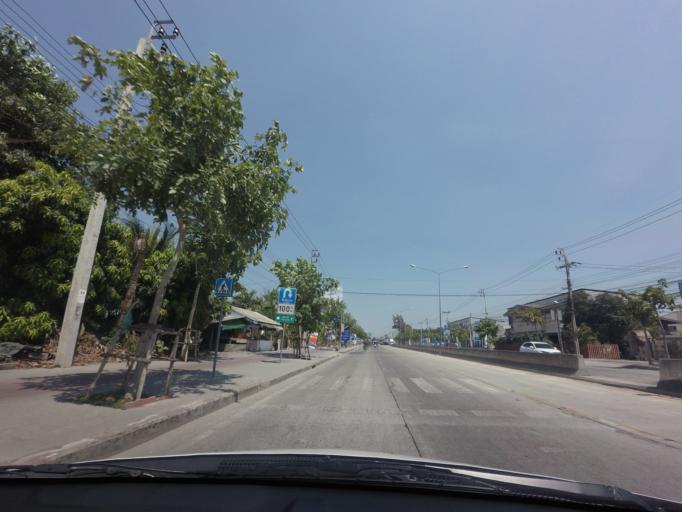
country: TH
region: Bangkok
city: Nong Chok
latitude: 13.8558
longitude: 100.8516
